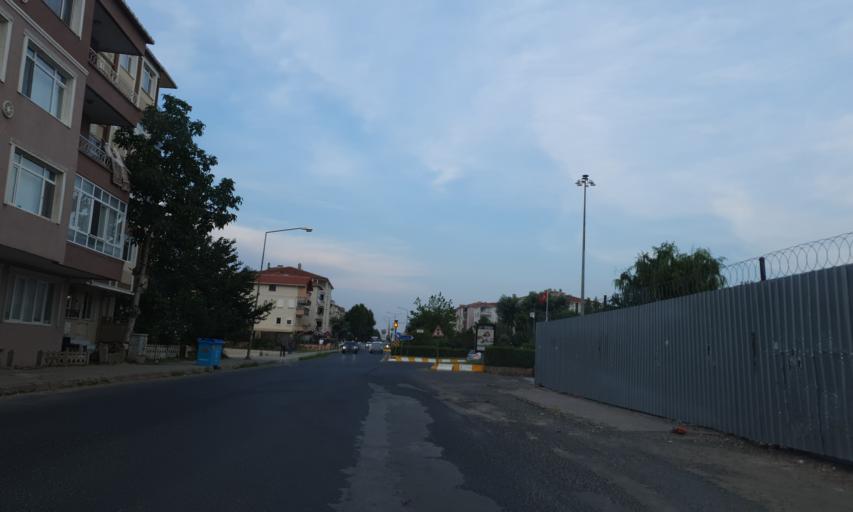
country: TR
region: Kirklareli
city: Luleburgaz
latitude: 41.4033
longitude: 27.3649
